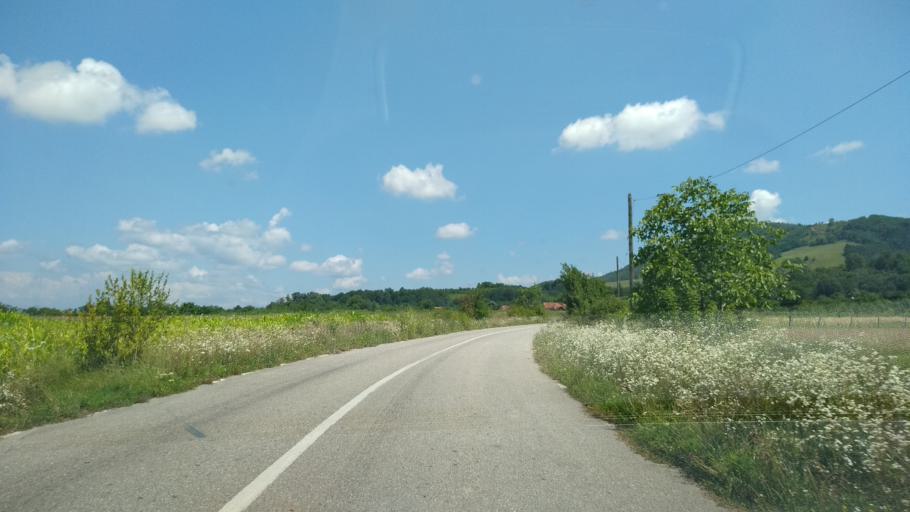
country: RO
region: Hunedoara
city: Berca
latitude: 45.6295
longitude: 23.0282
